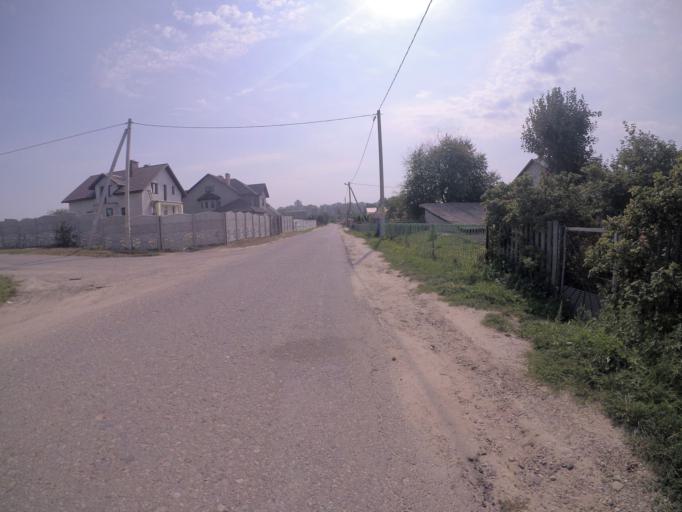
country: BY
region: Grodnenskaya
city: Hrodna
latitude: 53.7210
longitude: 23.8471
